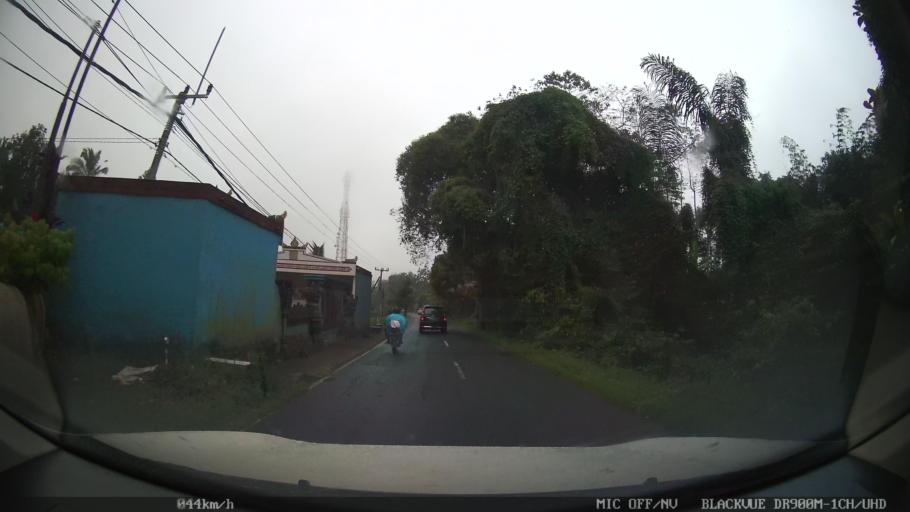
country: ID
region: Bali
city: Banjar Taro Kelod
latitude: -8.3595
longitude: 115.2733
